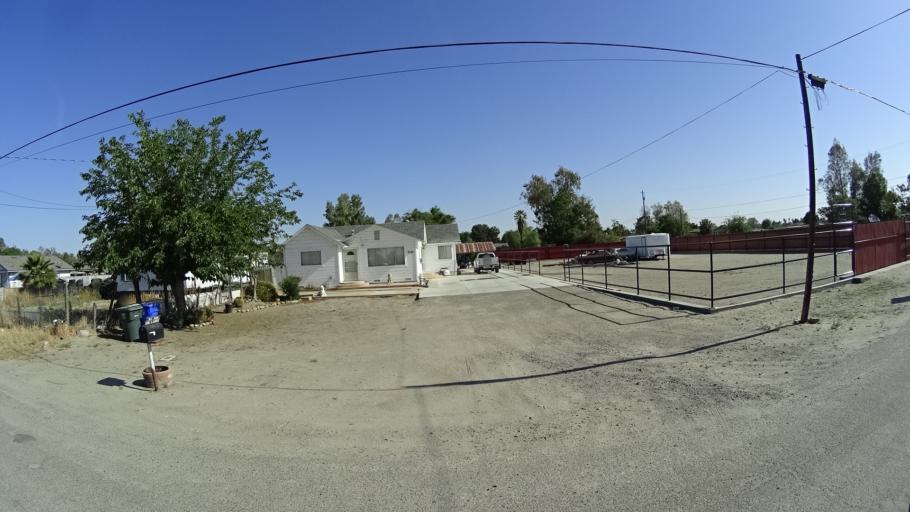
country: US
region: California
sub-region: Kings County
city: Corcoran
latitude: 36.0944
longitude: -119.5905
